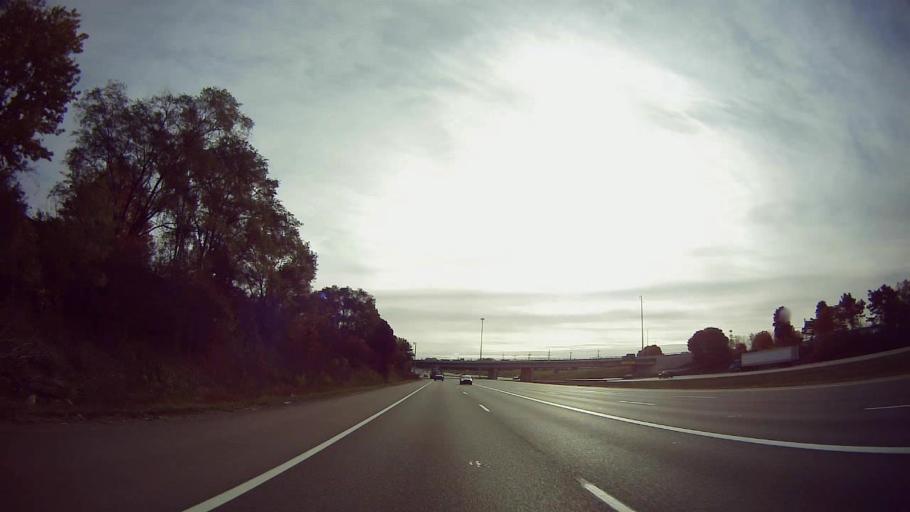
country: US
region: Michigan
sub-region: Wayne County
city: Plymouth
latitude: 42.3853
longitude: -83.4293
